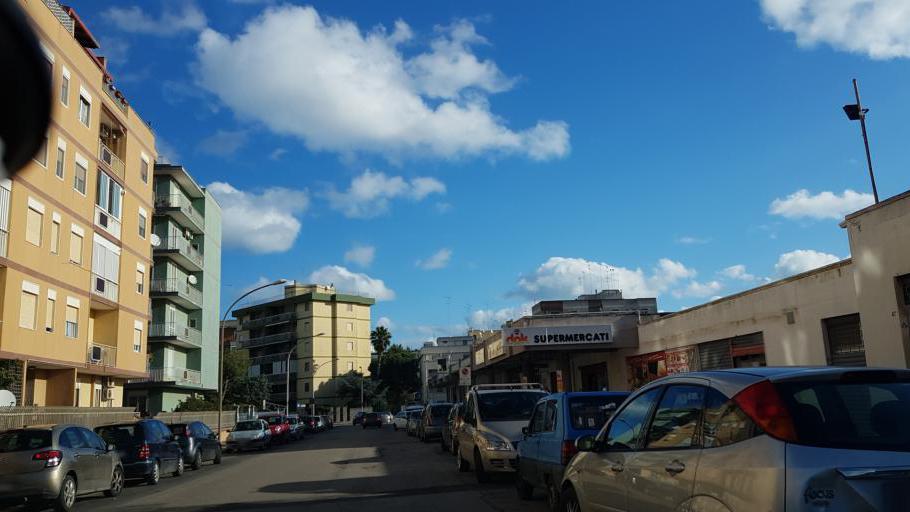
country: IT
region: Apulia
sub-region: Provincia di Brindisi
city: Brindisi
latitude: 40.6241
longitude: 17.9259
